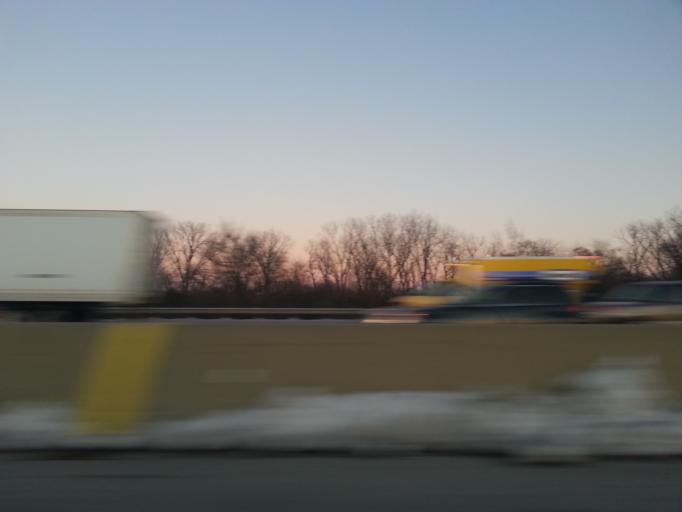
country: US
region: Illinois
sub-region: Cook County
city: University Park
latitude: 41.6088
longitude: -87.6820
